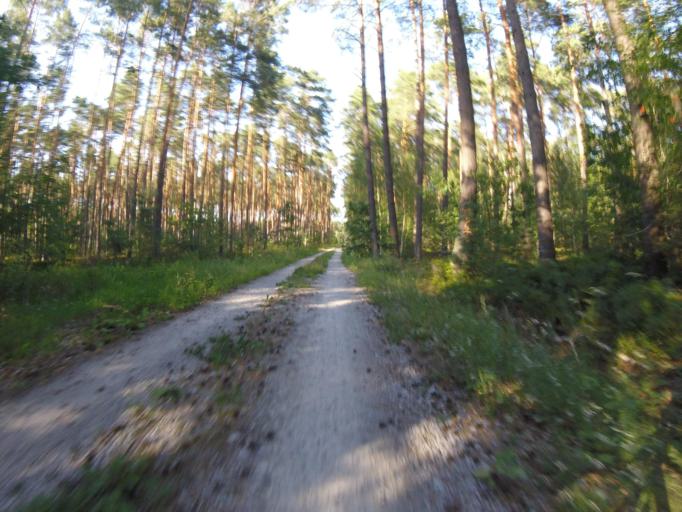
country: DE
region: Brandenburg
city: Erkner
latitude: 52.3337
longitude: 13.7395
